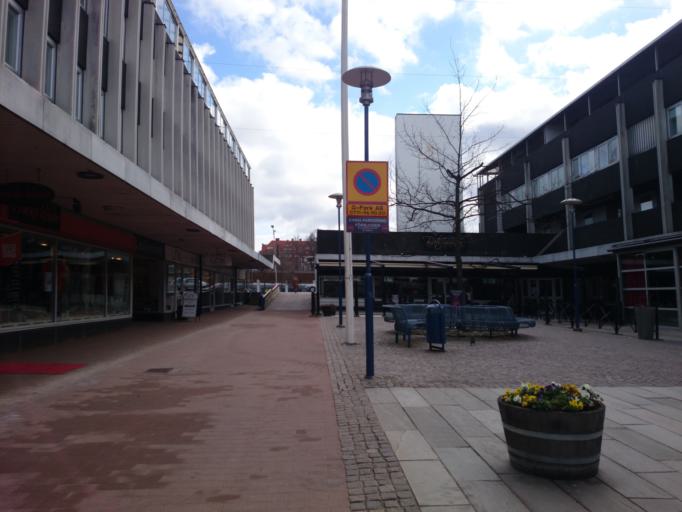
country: SE
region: Kronoberg
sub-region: Vaxjo Kommun
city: Vaexjoe
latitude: 56.8778
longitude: 14.8052
